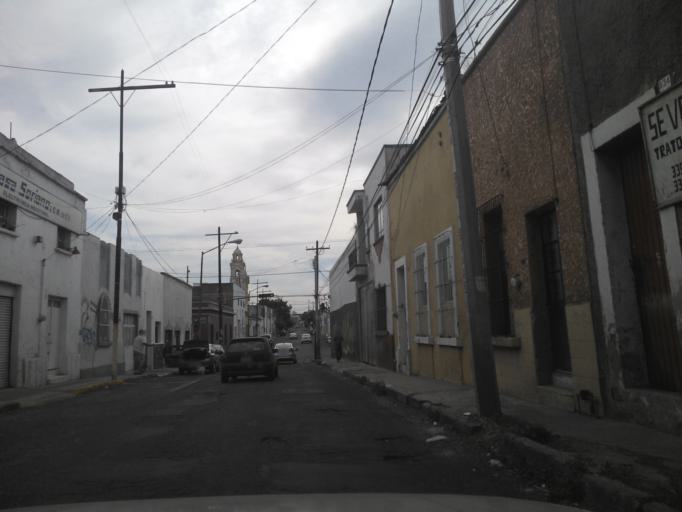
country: MX
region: Jalisco
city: Guadalajara
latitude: 20.6646
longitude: -103.3541
